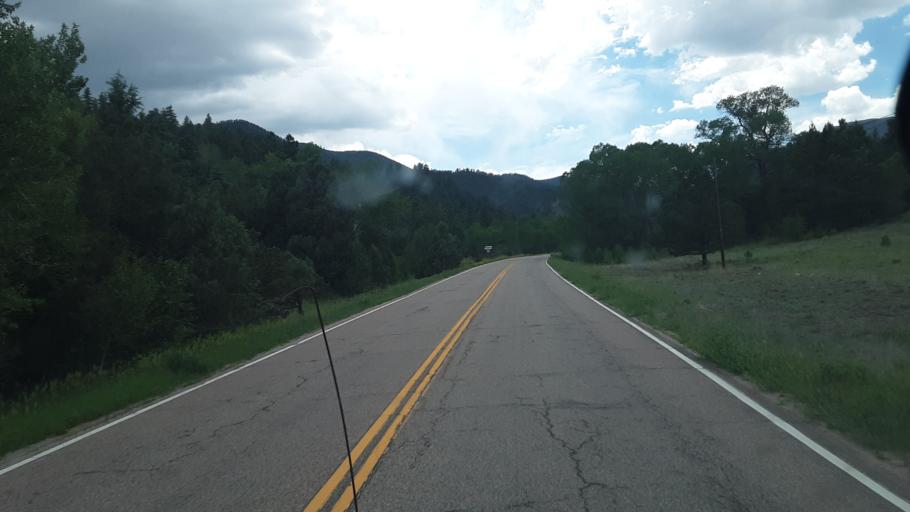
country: US
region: Colorado
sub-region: Fremont County
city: Florence
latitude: 38.1782
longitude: -105.1153
